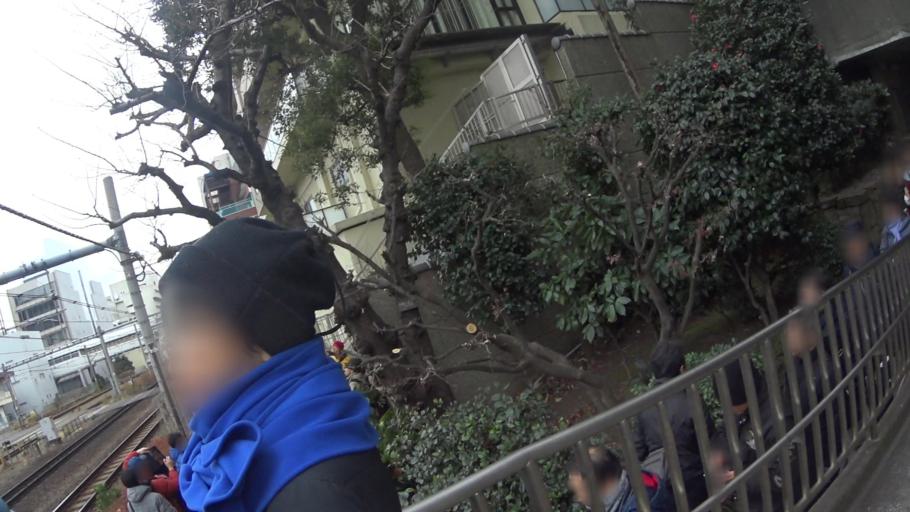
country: JP
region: Kanagawa
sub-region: Kawasaki-shi
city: Kawasaki
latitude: 35.5907
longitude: 139.7290
